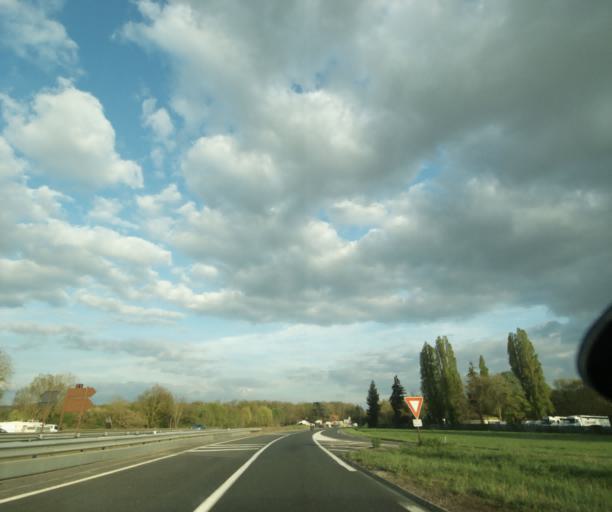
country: FR
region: Ile-de-France
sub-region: Departement de Seine-et-Marne
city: Chailly-en-Biere
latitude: 48.4547
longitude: 2.6182
